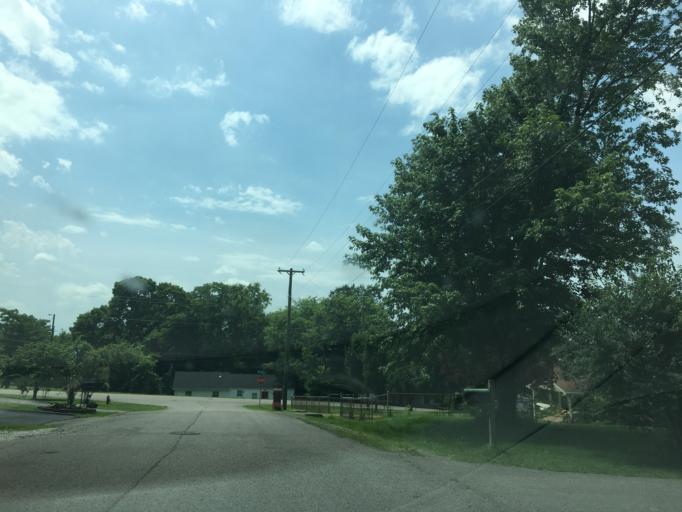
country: US
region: Tennessee
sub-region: Davidson County
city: Oak Hill
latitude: 36.1265
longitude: -86.7605
